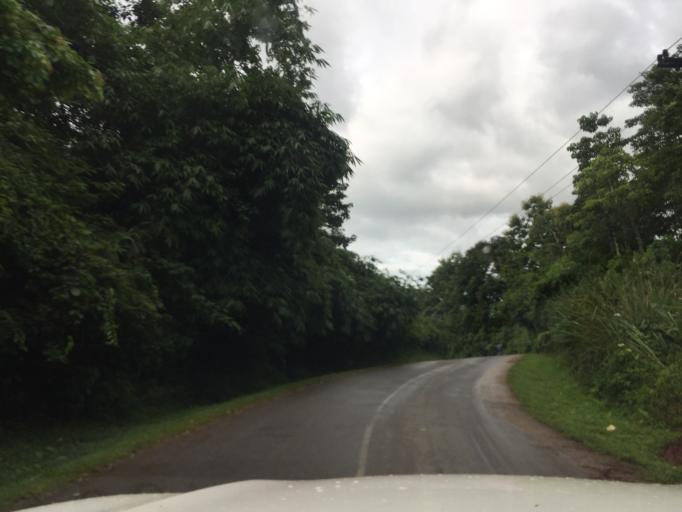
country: LA
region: Oudomxai
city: Muang La
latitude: 20.8015
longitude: 102.0874
